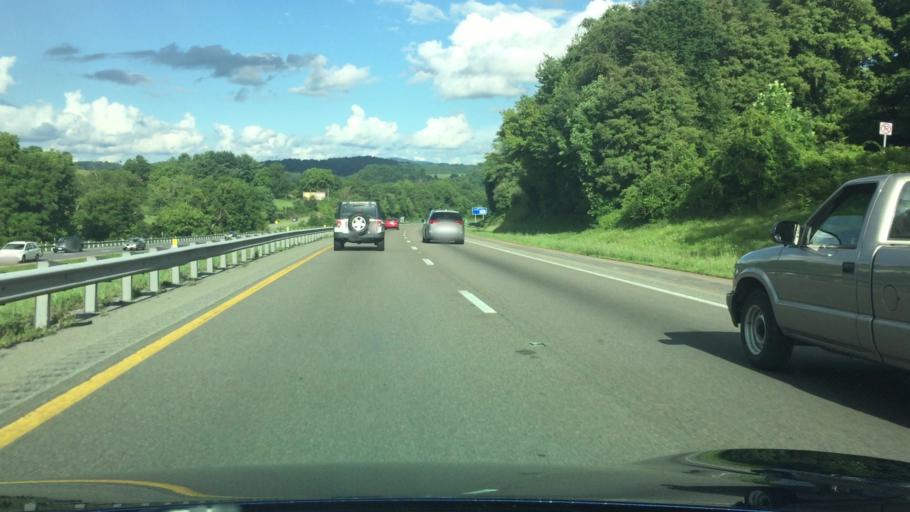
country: US
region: Virginia
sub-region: Smyth County
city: Chilhowie
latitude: 36.7883
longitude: -81.7090
